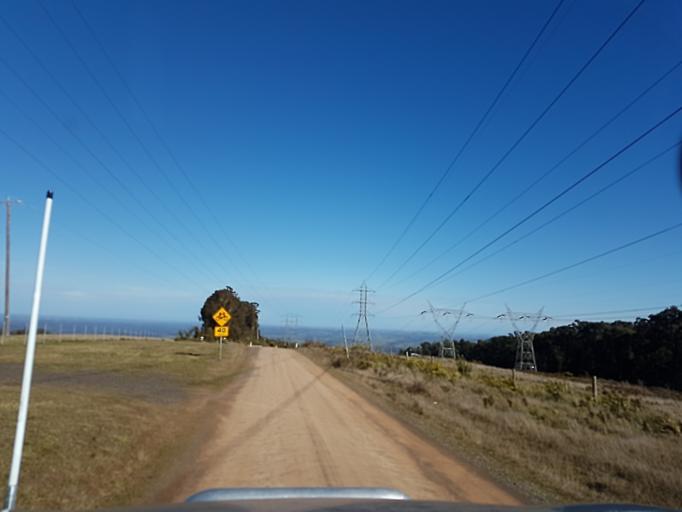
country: AU
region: Victoria
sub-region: Murrindindi
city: Kinglake West
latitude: -37.5162
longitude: 145.3132
